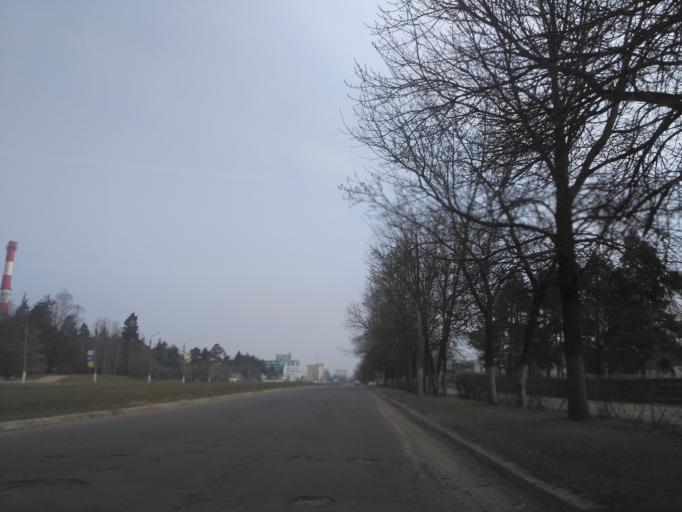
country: BY
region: Minsk
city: Horad Barysaw
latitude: 54.2002
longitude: 28.4972
